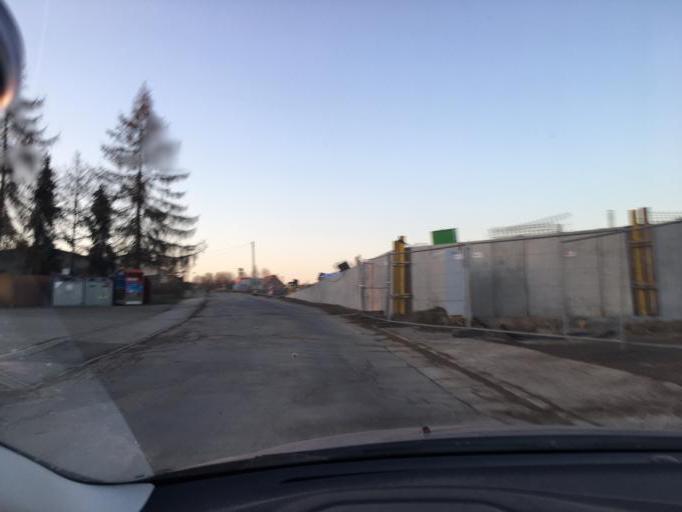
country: DE
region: Saxony
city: Lunzenau
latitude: 50.9646
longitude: 12.7512
